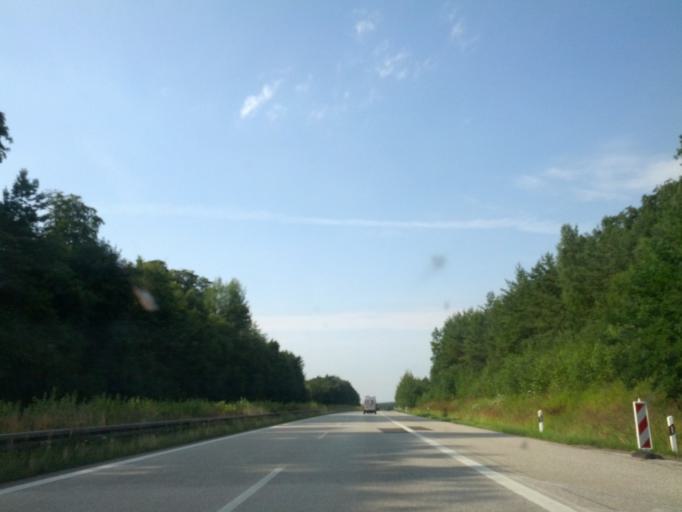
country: DE
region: Mecklenburg-Vorpommern
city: Lalendorf
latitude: 53.7482
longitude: 12.3313
